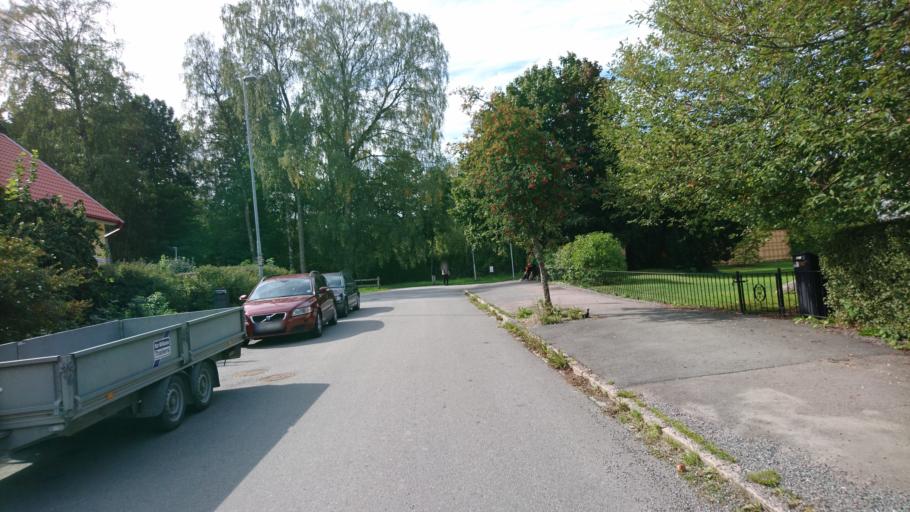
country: SE
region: Uppsala
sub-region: Uppsala Kommun
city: Uppsala
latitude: 59.8445
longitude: 17.6267
